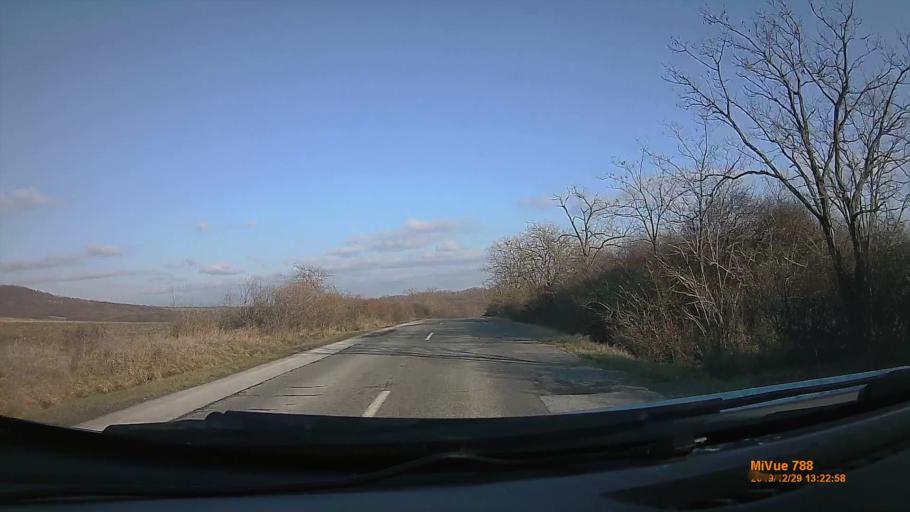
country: HU
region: Heves
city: Domoszlo
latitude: 47.8489
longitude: 20.1639
